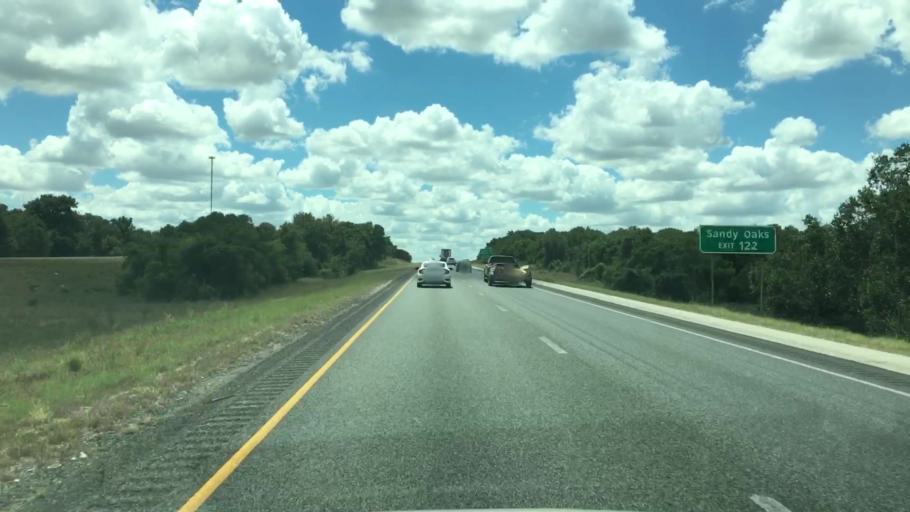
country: US
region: Texas
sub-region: Bexar County
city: Elmendorf
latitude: 29.1925
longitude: -98.4229
